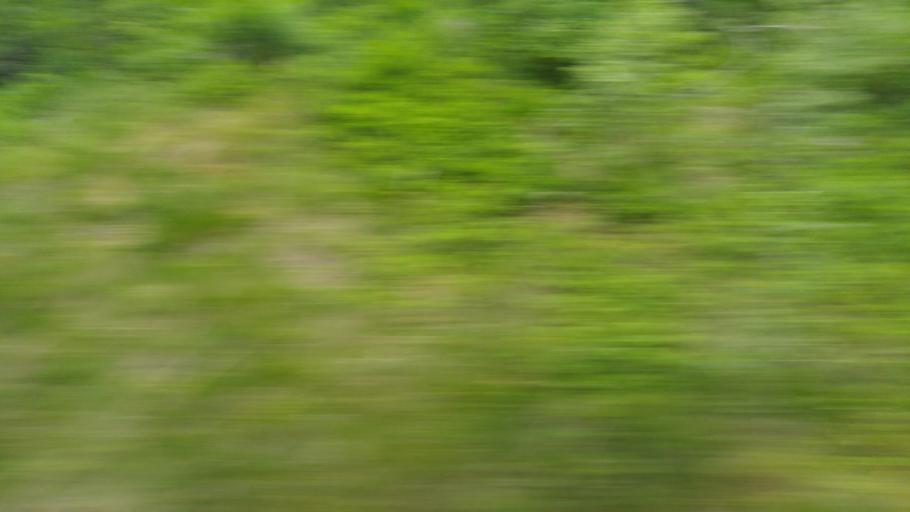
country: NO
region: Nord-Trondelag
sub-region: Levanger
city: Skogn
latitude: 63.4575
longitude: 11.3035
